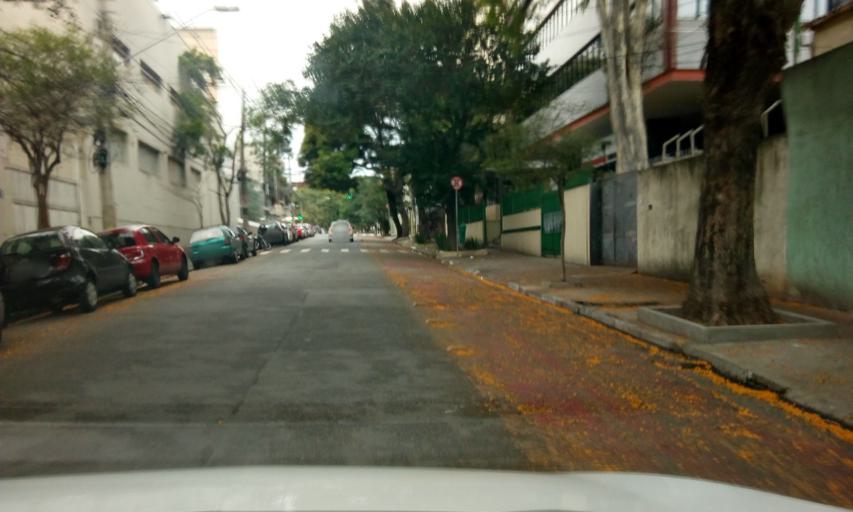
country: BR
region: Sao Paulo
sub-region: Sao Paulo
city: Sao Paulo
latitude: -23.5305
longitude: -46.6482
